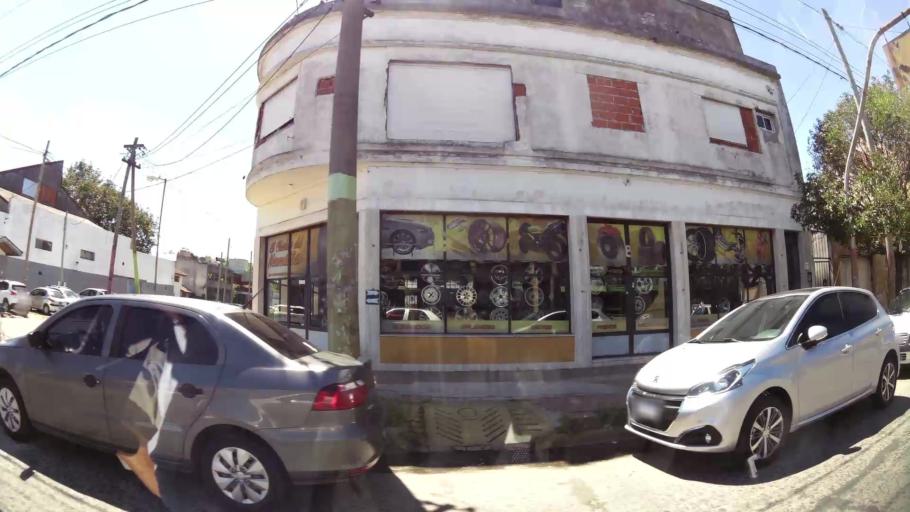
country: AR
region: Buenos Aires
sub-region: Partido de Quilmes
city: Quilmes
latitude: -34.7228
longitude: -58.2711
